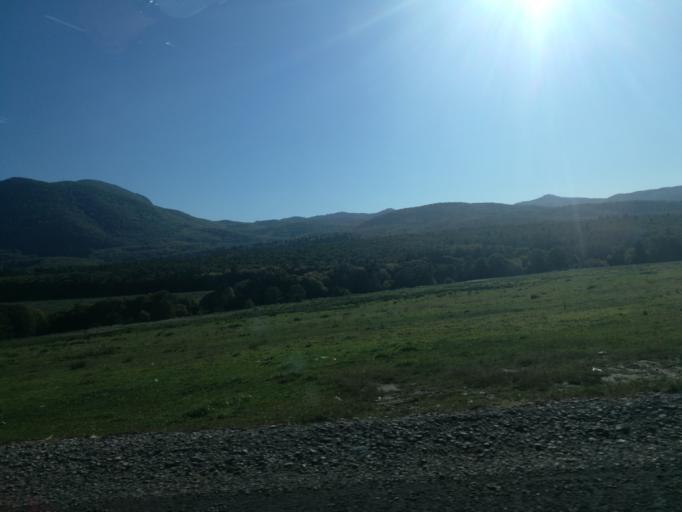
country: RO
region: Brasov
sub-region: Comuna Dumbravita
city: Dumbravita
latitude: 45.7496
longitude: 25.4057
